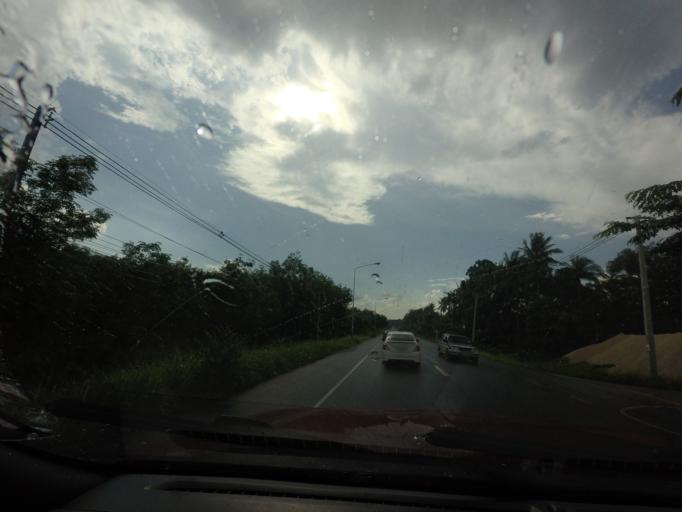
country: TH
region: Pattani
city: Mae Lan
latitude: 6.6592
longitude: 101.1695
